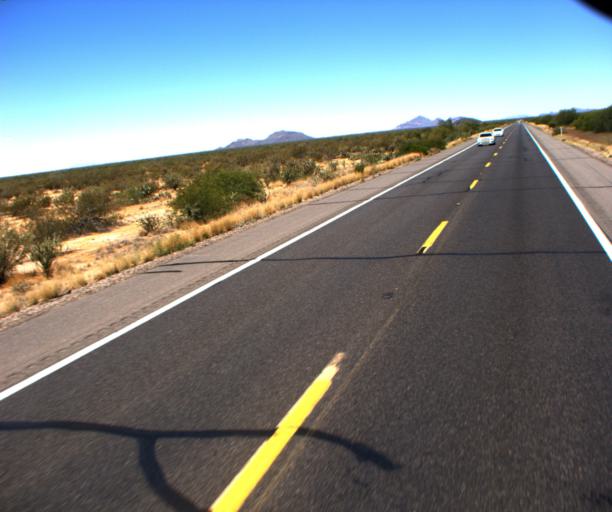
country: US
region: Arizona
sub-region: Yavapai County
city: Congress
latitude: 34.1559
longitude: -112.9973
